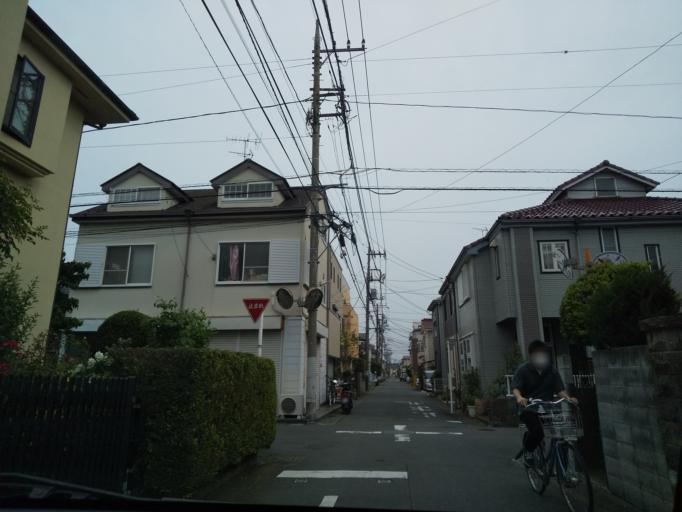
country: JP
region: Kanagawa
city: Minami-rinkan
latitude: 35.4660
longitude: 139.4258
